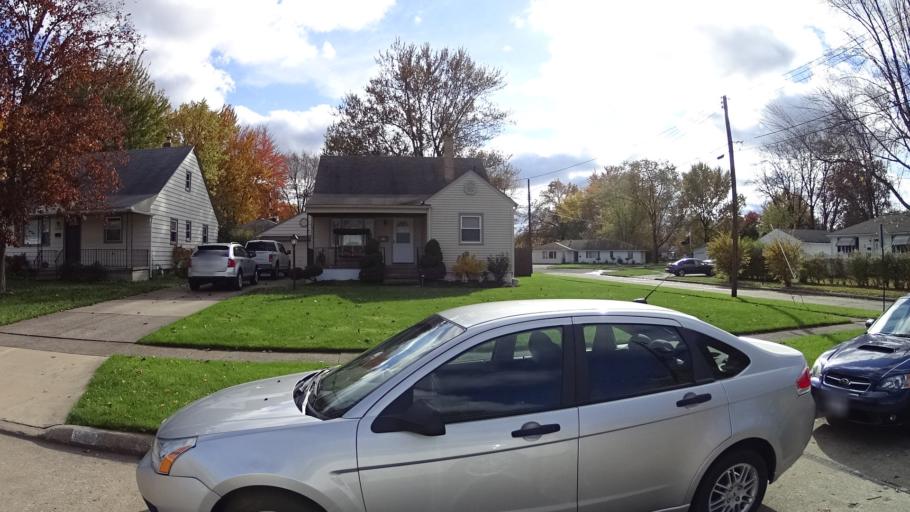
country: US
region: Ohio
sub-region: Lorain County
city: Lorain
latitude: 41.4388
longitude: -82.1882
